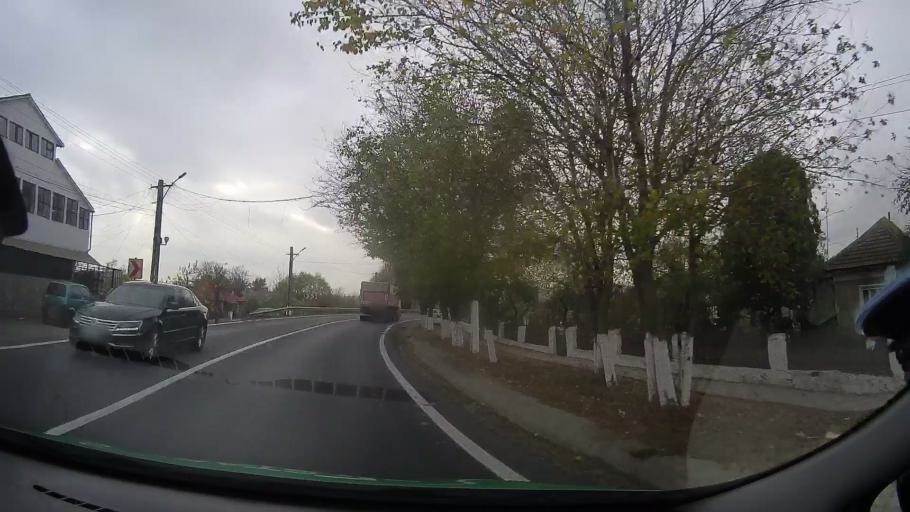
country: RO
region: Constanta
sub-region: Comuna Castelu
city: Castelu
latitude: 44.2530
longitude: 28.3314
